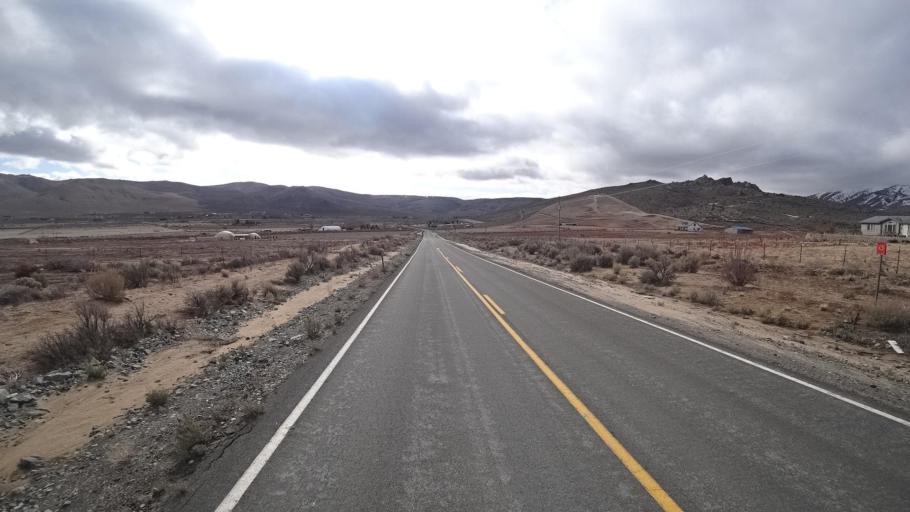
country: US
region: Nevada
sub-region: Washoe County
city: Cold Springs
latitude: 39.8659
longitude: -119.9443
